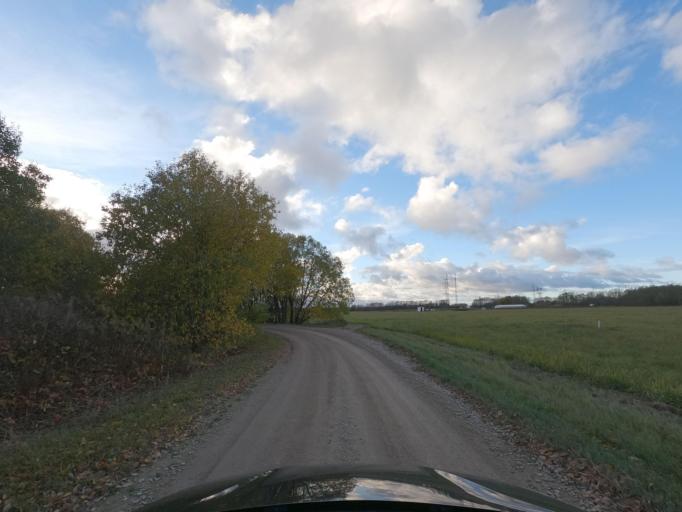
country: EE
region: Harju
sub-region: Saue vald
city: Laagri
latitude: 59.3703
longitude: 24.5782
